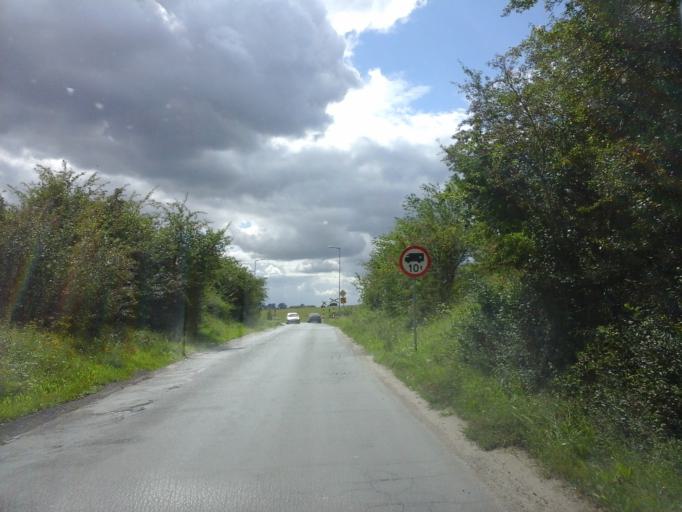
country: PL
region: West Pomeranian Voivodeship
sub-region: Powiat policki
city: Przeclaw
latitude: 53.4130
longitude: 14.4232
